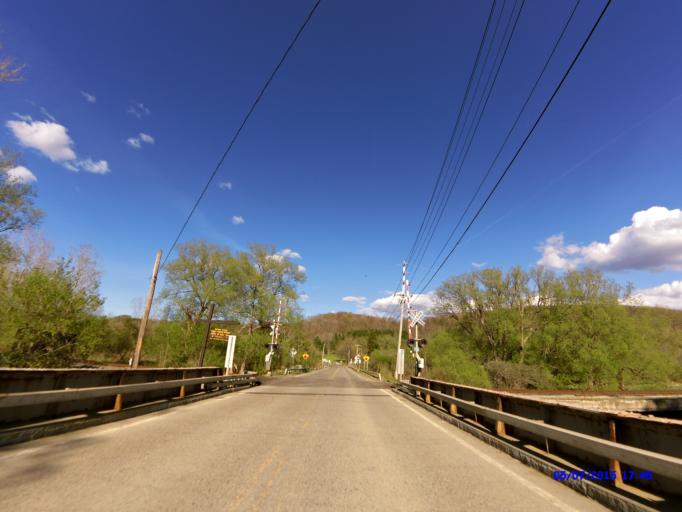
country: US
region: New York
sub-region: Cattaraugus County
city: Franklinville
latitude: 42.3209
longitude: -78.4647
